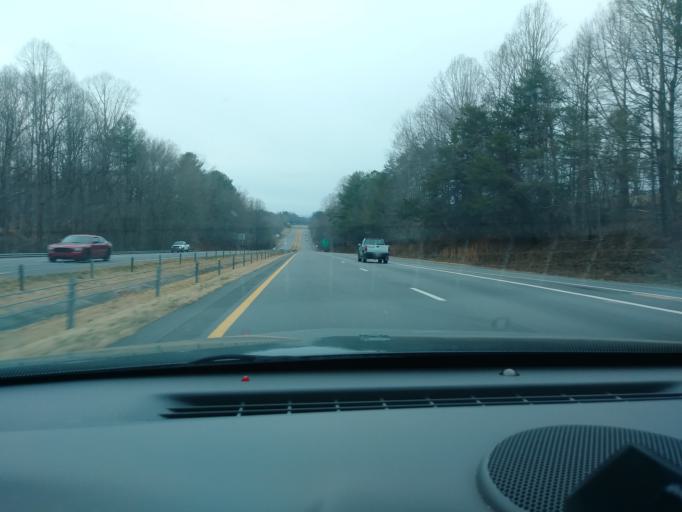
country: US
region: North Carolina
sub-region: Wilkes County
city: Wilkesboro
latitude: 36.1350
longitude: -81.1493
